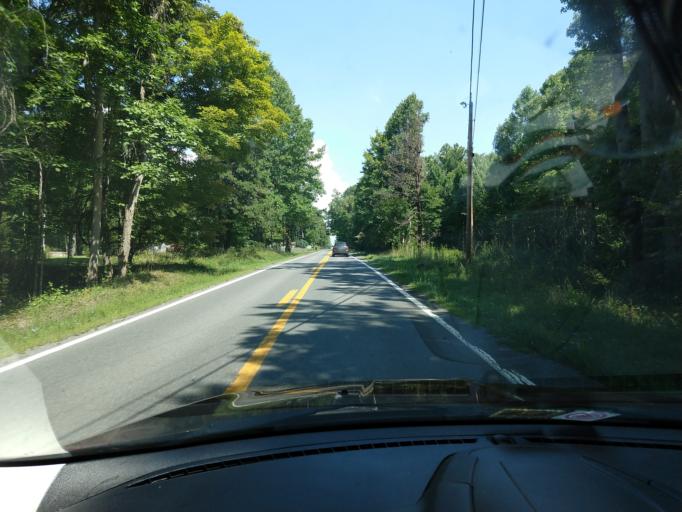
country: US
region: West Virginia
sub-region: Greenbrier County
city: Fairlea
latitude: 37.8345
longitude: -80.5558
